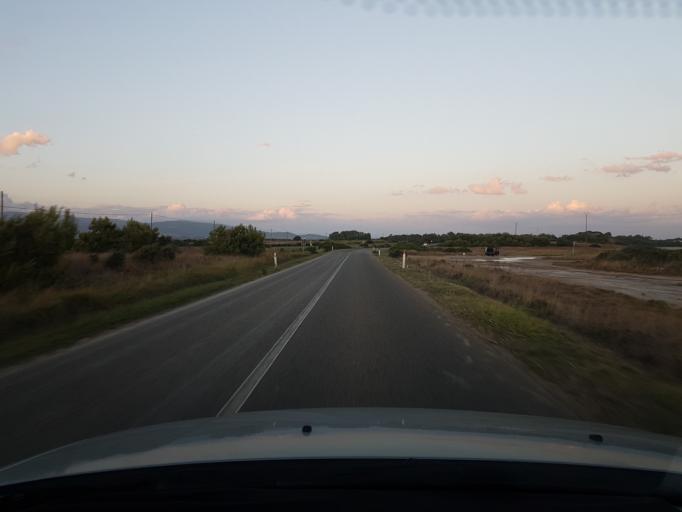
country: IT
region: Sardinia
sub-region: Provincia di Oristano
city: Riola Sardo
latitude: 40.0253
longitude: 8.4355
